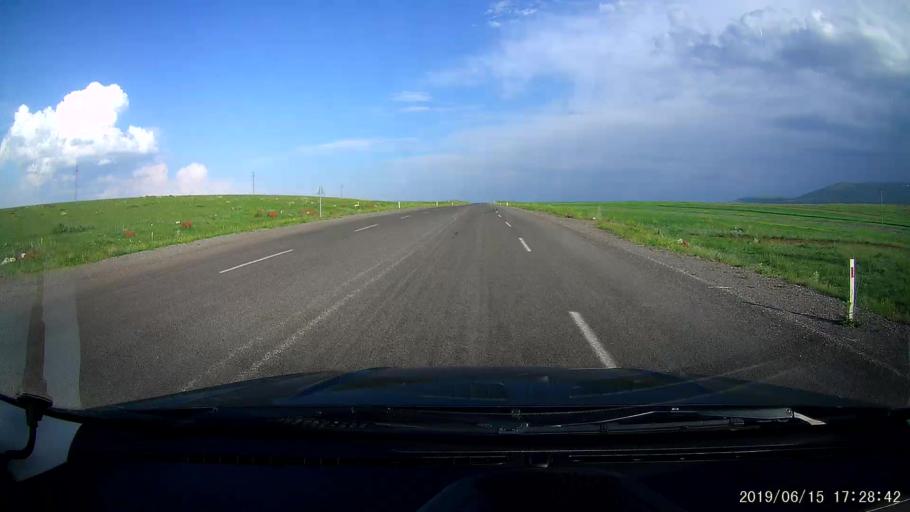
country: TR
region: Kars
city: Basgedikler
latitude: 40.5942
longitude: 43.4463
